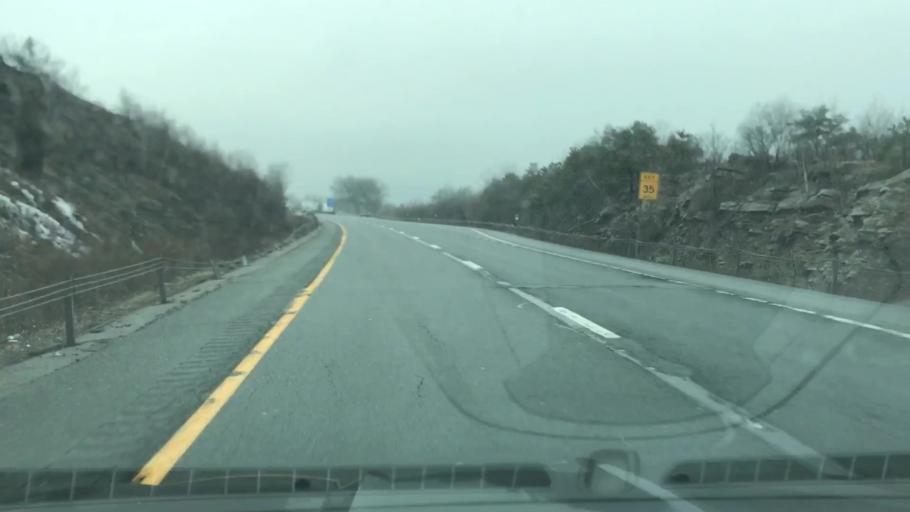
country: US
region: New York
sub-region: Orange County
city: Port Jervis
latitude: 41.3743
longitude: -74.6352
